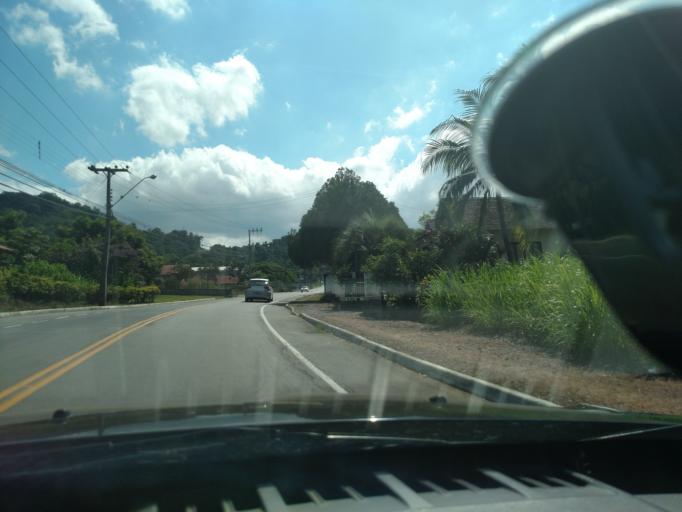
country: BR
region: Santa Catarina
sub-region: Indaial
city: Indaial
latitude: -26.8891
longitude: -49.2105
